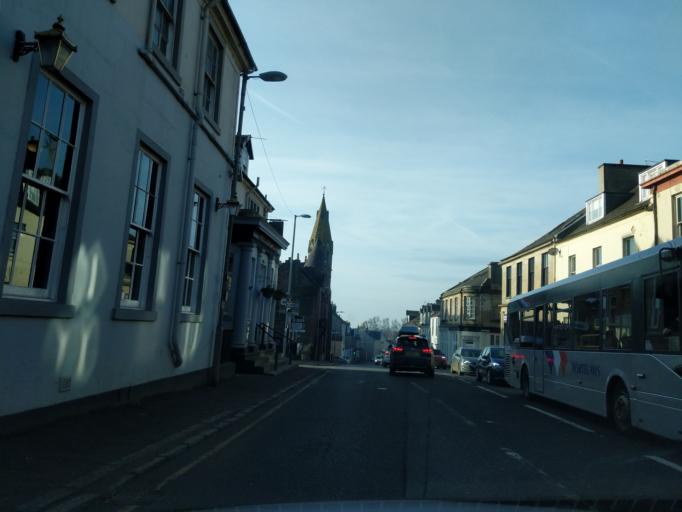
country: GB
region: Scotland
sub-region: South Lanarkshire
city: Lanark
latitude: 55.6738
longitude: -3.7811
